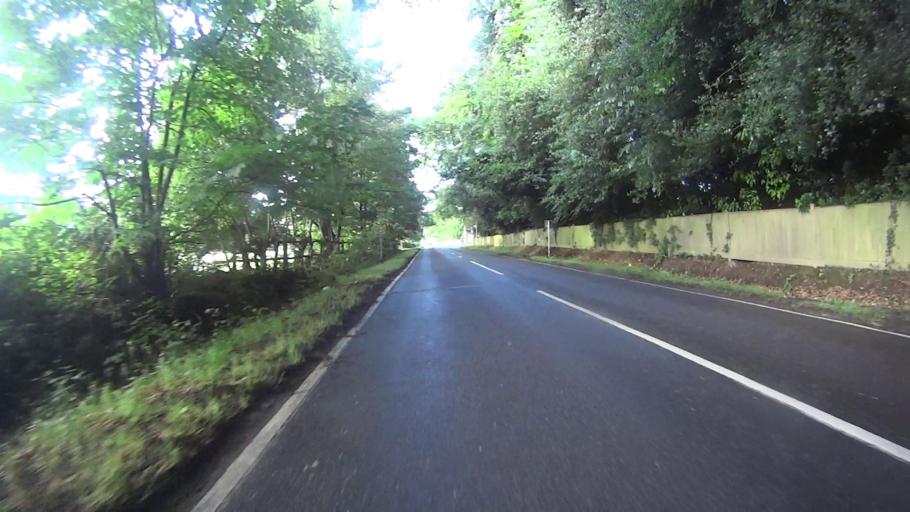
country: GB
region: England
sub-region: Surrey
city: Lingfield
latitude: 51.1616
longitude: -0.0217
